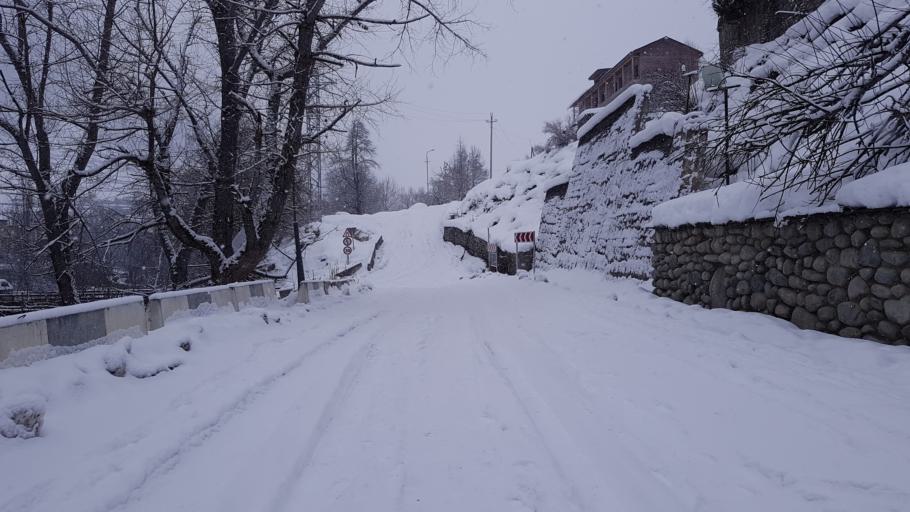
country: GE
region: Samegrelo and Zemo Svaneti
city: Mest'ia
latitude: 43.0421
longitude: 42.7277
